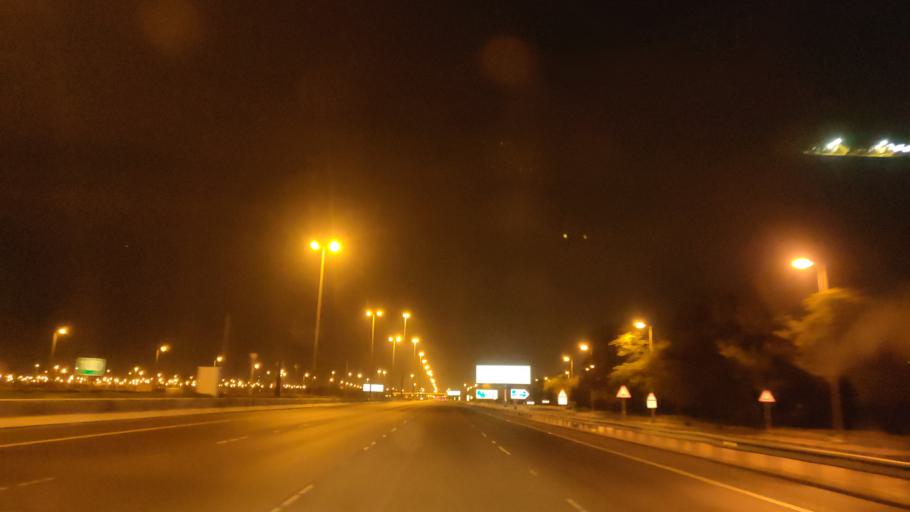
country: KW
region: Al Farwaniyah
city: Janub as Surrah
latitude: 29.3049
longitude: 47.9913
